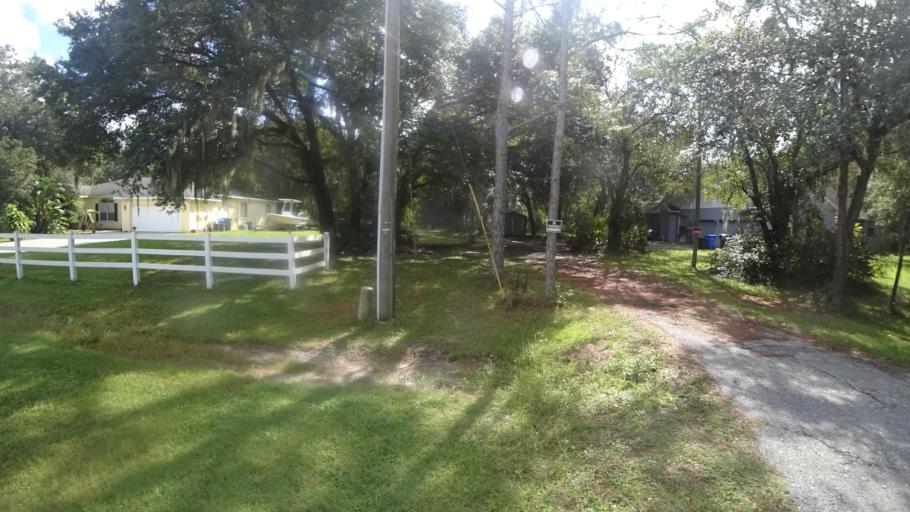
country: US
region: Florida
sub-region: Hillsborough County
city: Ruskin
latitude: 27.6478
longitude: -82.4081
